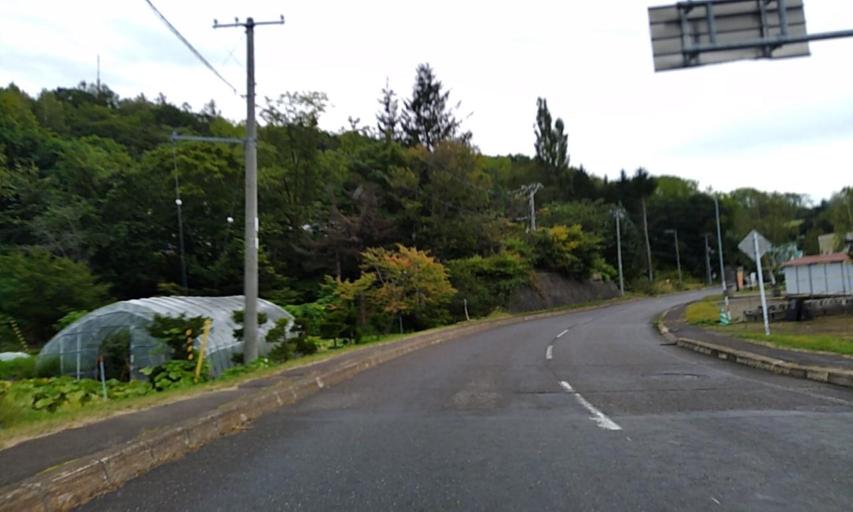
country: JP
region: Hokkaido
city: Abashiri
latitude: 44.0039
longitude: 144.2308
